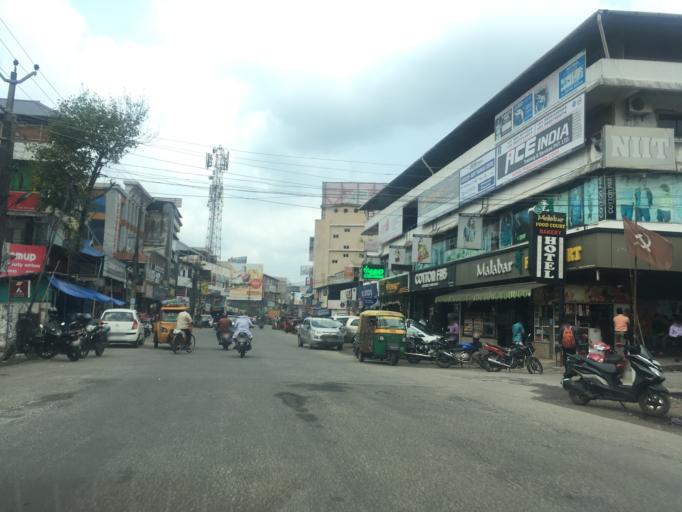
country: IN
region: Kerala
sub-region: Ernakulam
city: Elur
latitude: 10.0269
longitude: 76.3116
